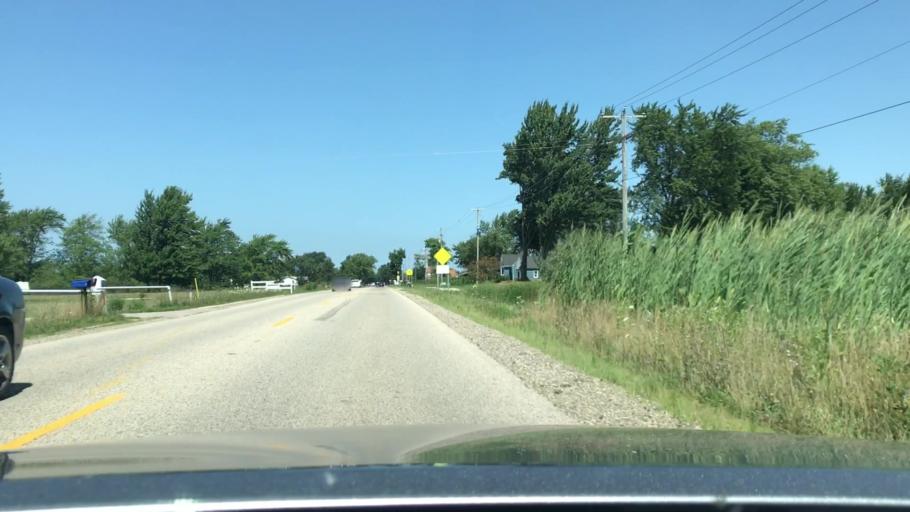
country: US
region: Michigan
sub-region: Ottawa County
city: Holland
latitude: 42.8508
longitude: -86.0791
